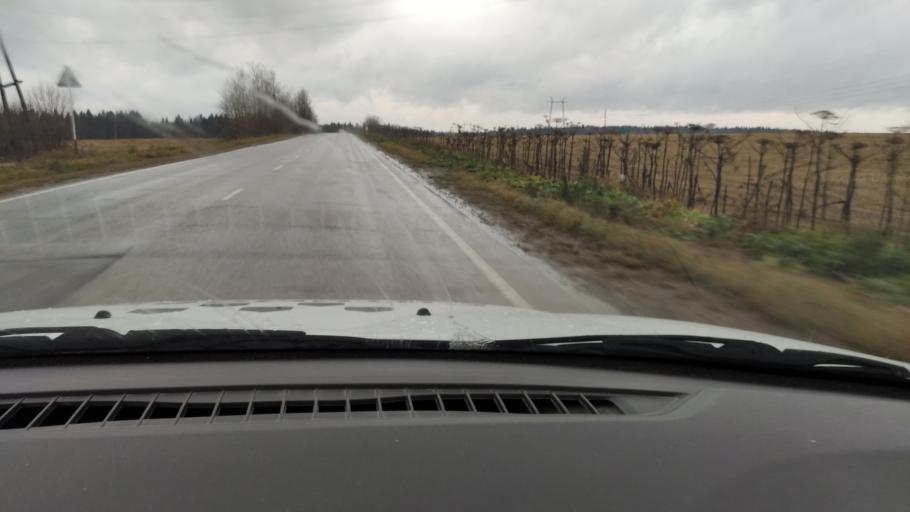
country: RU
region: Perm
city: Sylva
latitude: 58.0295
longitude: 56.6976
